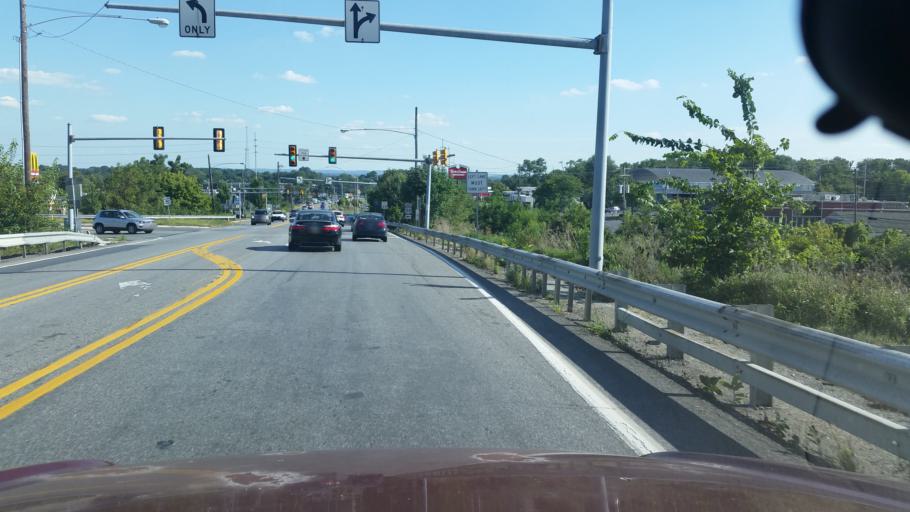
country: US
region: Pennsylvania
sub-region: Lancaster County
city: Mountville
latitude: 40.0518
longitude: -76.3960
